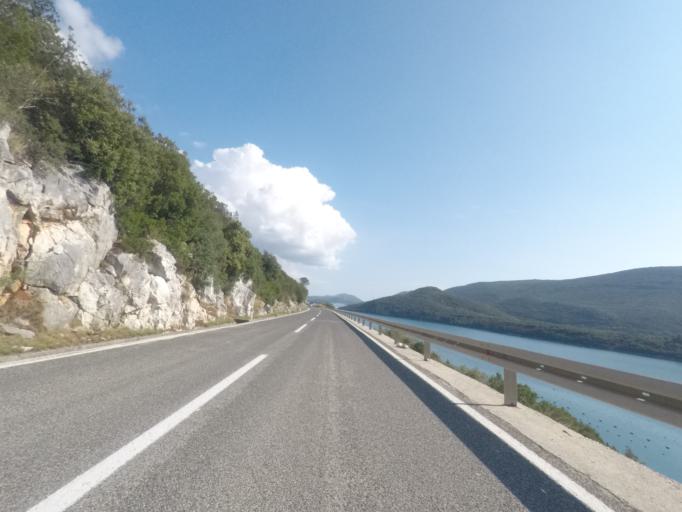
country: HR
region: Dubrovacko-Neretvanska
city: Ston
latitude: 42.8832
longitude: 17.6600
